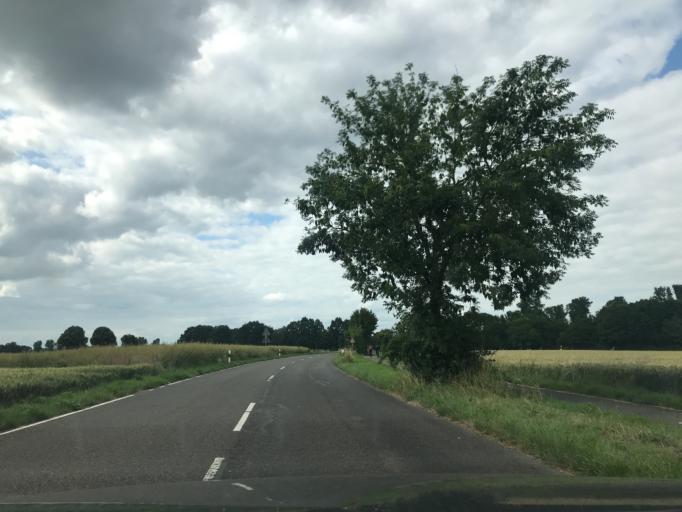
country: DE
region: North Rhine-Westphalia
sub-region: Regierungsbezirk Dusseldorf
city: Neuss
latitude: 51.1470
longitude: 6.7207
